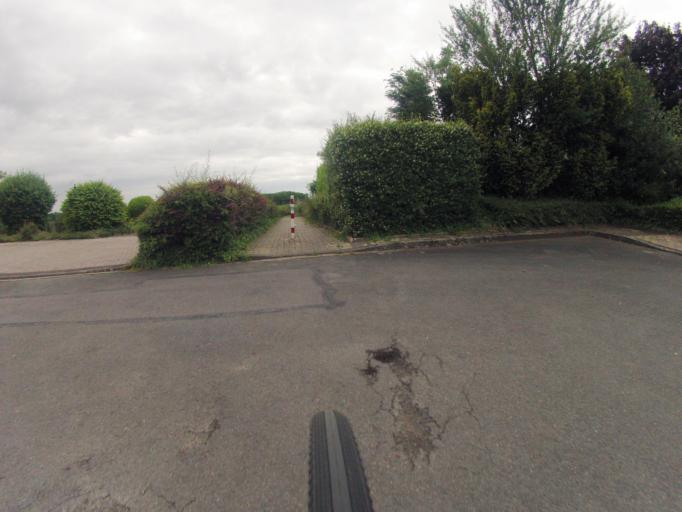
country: DE
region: North Rhine-Westphalia
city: Ibbenburen
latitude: 52.2256
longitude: 7.7339
